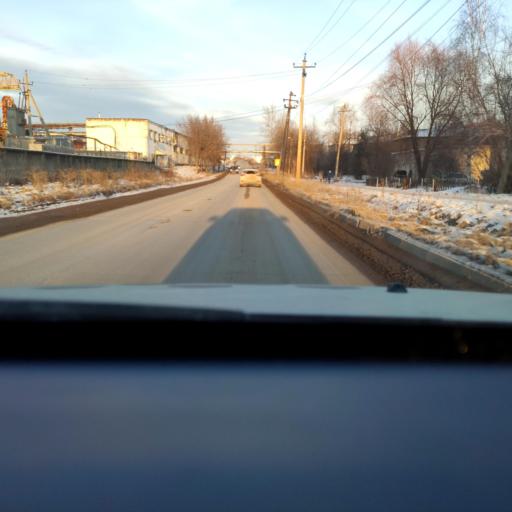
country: RU
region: Perm
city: Ferma
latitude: 57.9096
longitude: 56.3068
